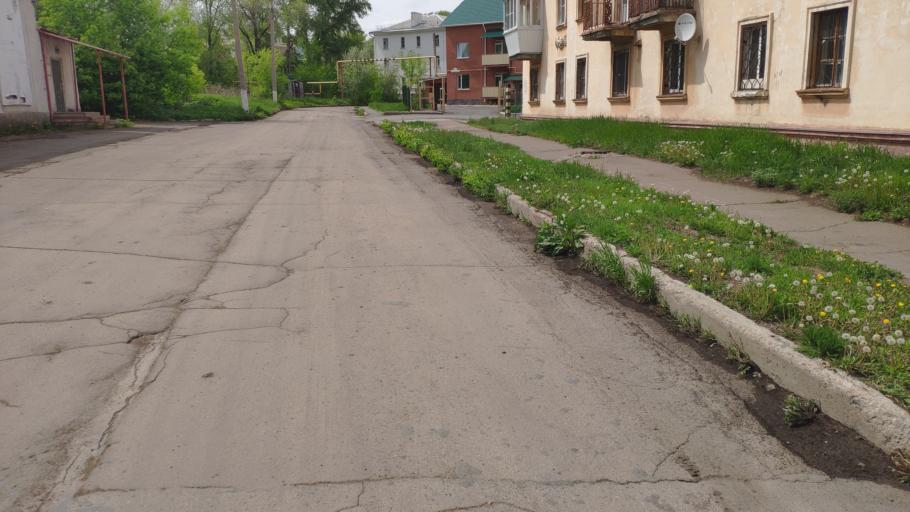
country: RU
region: Chelyabinsk
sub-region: Gorod Magnitogorsk
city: Magnitogorsk
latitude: 53.4190
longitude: 58.9575
